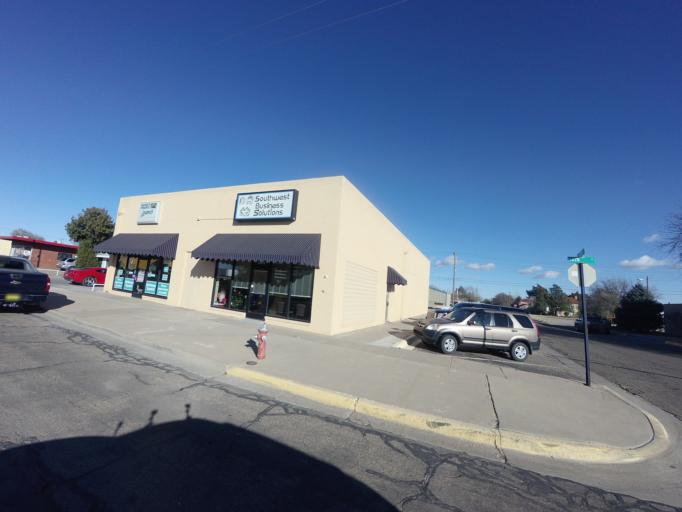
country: US
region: New Mexico
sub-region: Curry County
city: Clovis
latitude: 34.4101
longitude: -103.2053
